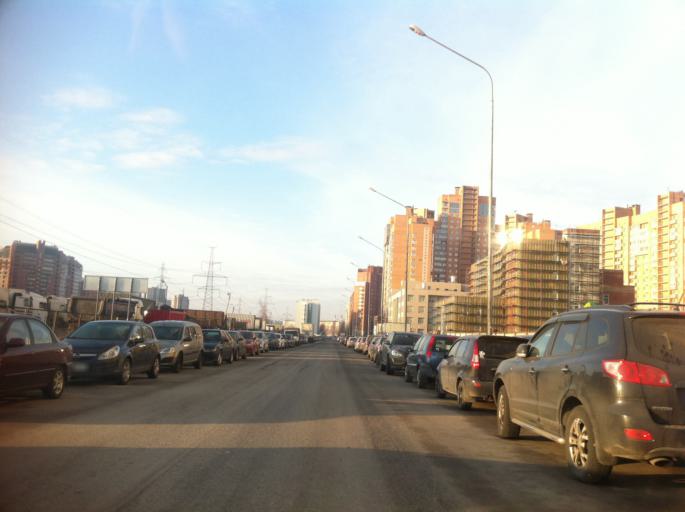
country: RU
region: St.-Petersburg
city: Uritsk
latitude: 59.8604
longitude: 30.2031
